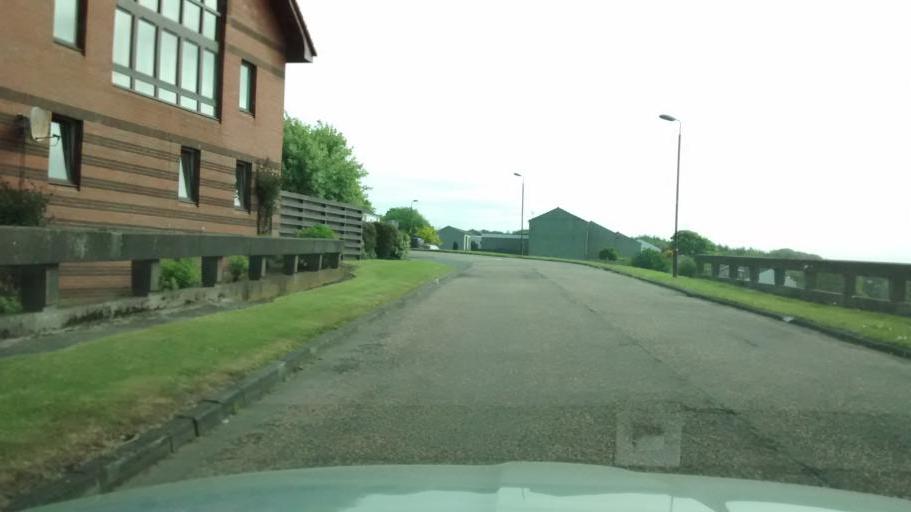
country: GB
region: Scotland
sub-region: West Lothian
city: Mid Calder
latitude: 55.8923
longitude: -3.4973
